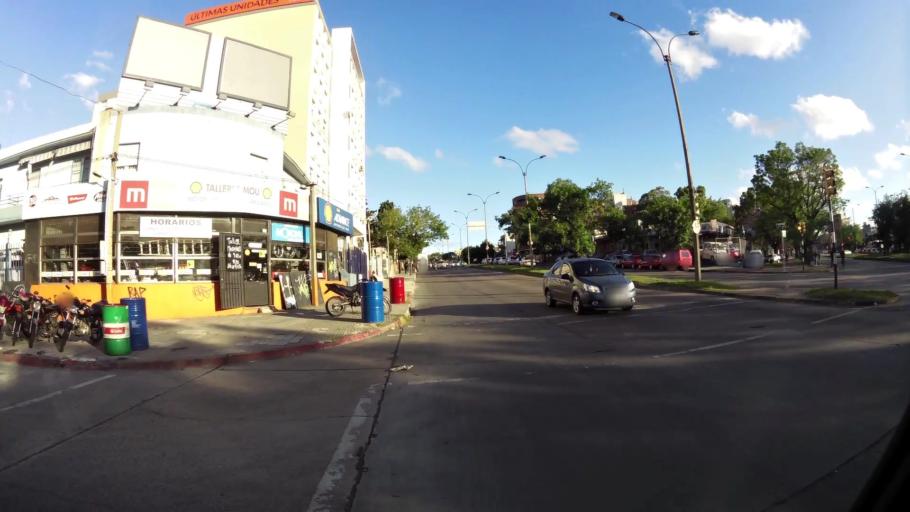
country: UY
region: Montevideo
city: Montevideo
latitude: -34.8759
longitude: -56.1522
